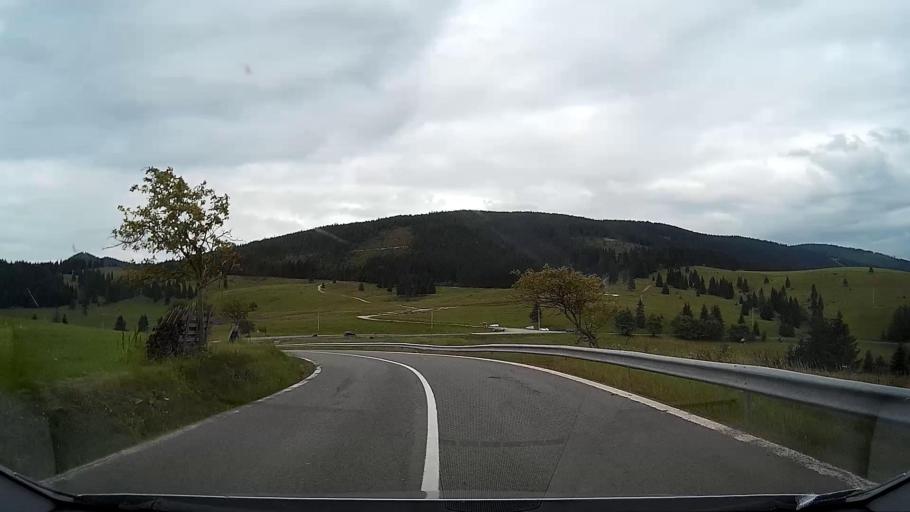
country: SK
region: Kosicky
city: Dobsina
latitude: 48.8635
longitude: 20.2252
